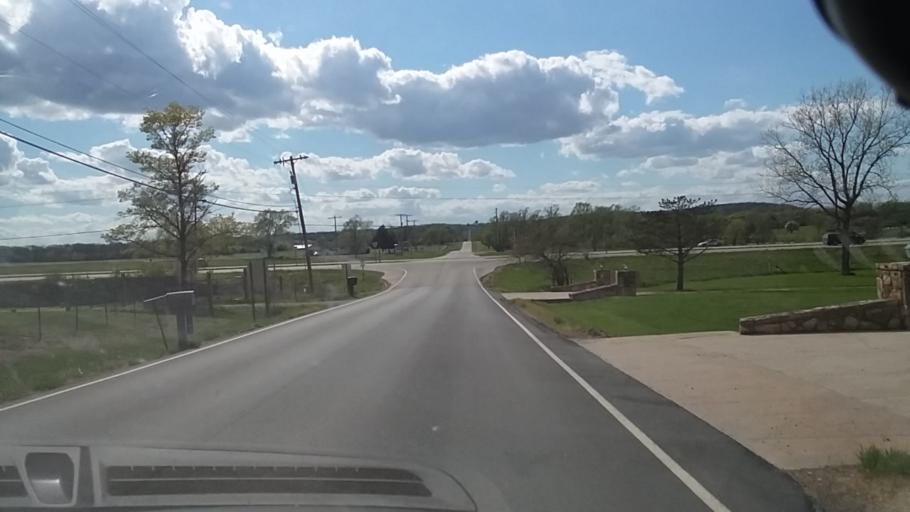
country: US
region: Kansas
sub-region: Douglas County
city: Lawrence
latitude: 38.8990
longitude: -95.2591
